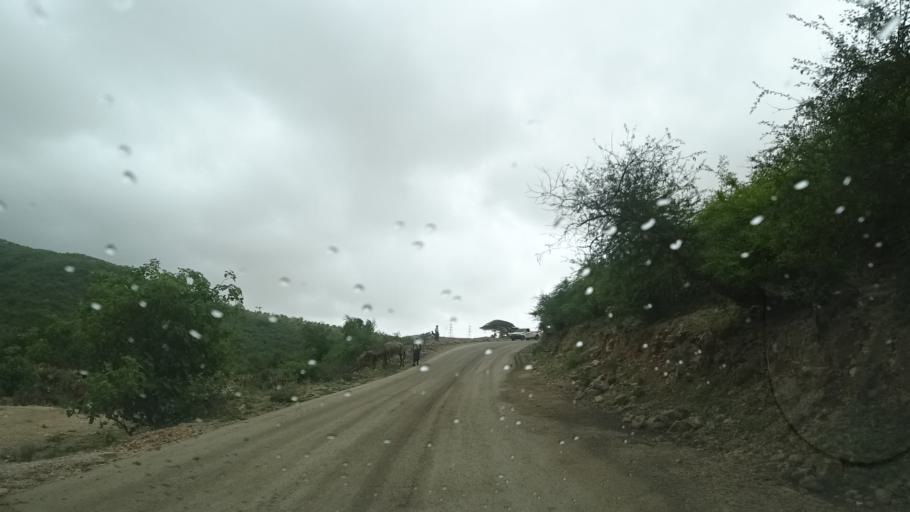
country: OM
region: Zufar
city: Salalah
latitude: 17.0955
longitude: 54.3330
